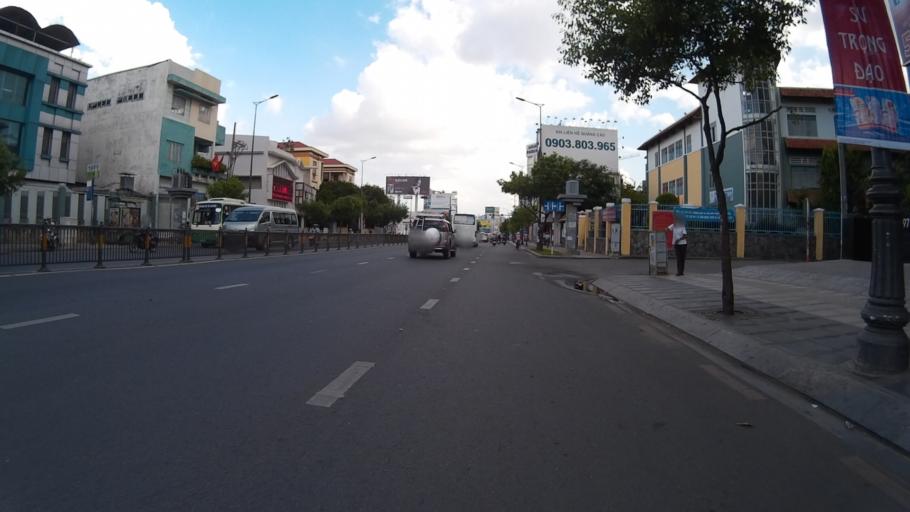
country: VN
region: Ho Chi Minh City
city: Quan Phu Nhuan
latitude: 10.7934
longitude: 106.6789
